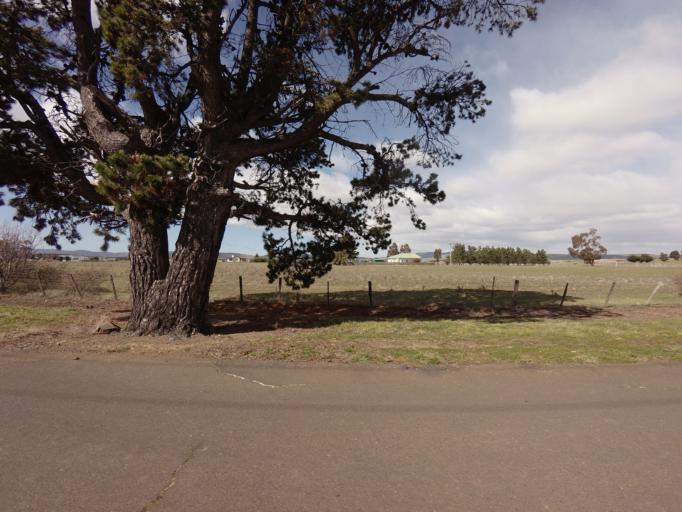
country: AU
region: Tasmania
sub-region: Northern Midlands
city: Evandale
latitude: -42.1385
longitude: 147.4256
